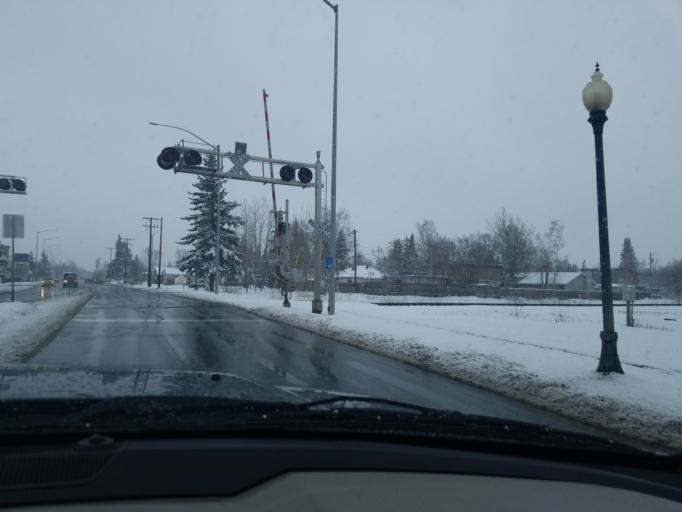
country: US
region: Alaska
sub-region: Anchorage Municipality
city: Anchorage
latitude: 61.1856
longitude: -149.9212
